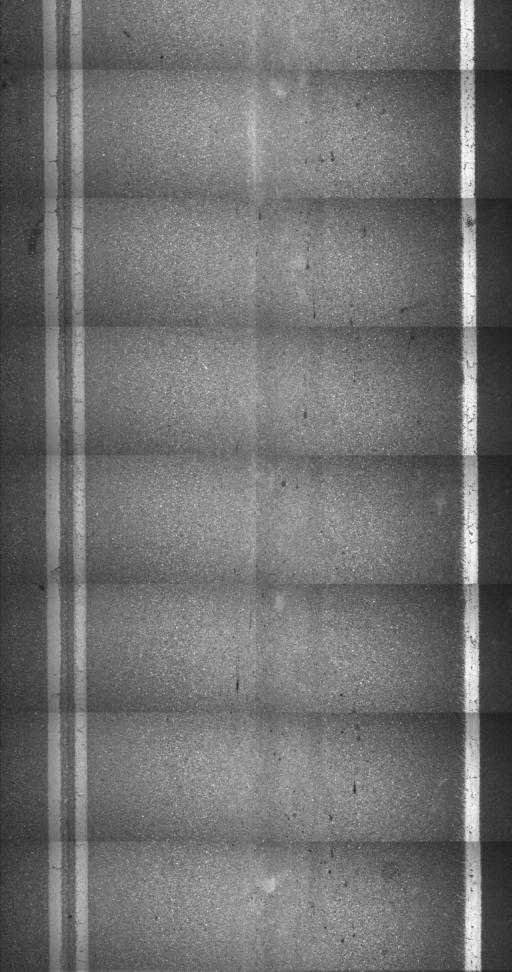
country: US
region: Vermont
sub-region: Addison County
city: Vergennes
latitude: 44.1081
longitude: -73.2190
